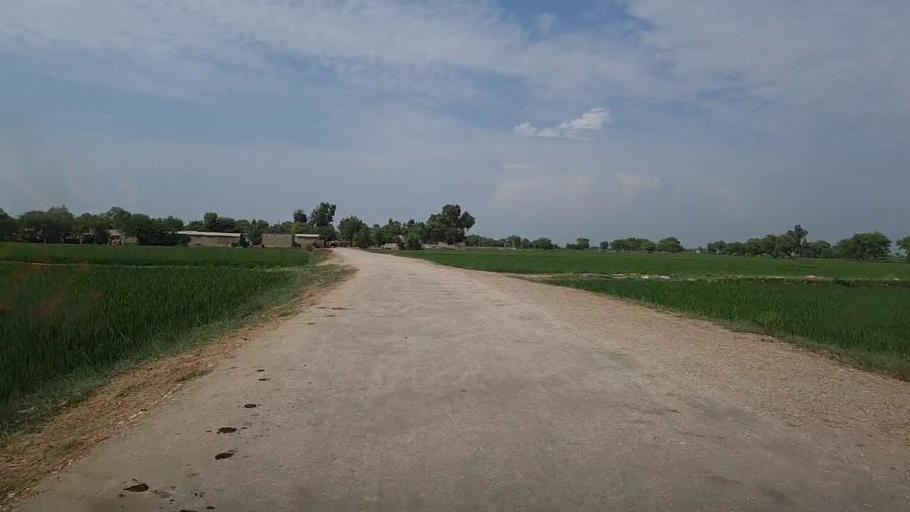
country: PK
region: Sindh
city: Thul
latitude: 28.2437
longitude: 68.8101
